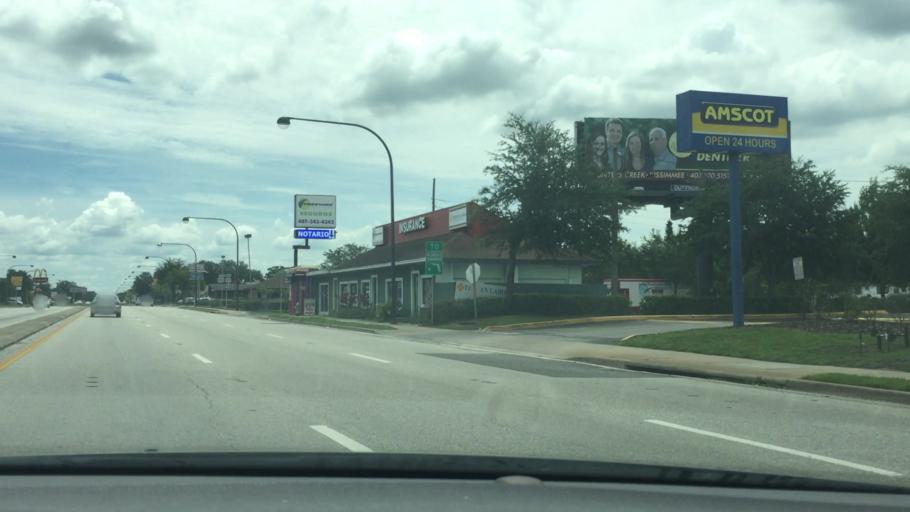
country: US
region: Florida
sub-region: Osceola County
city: Kissimmee
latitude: 28.3043
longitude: -81.4154
